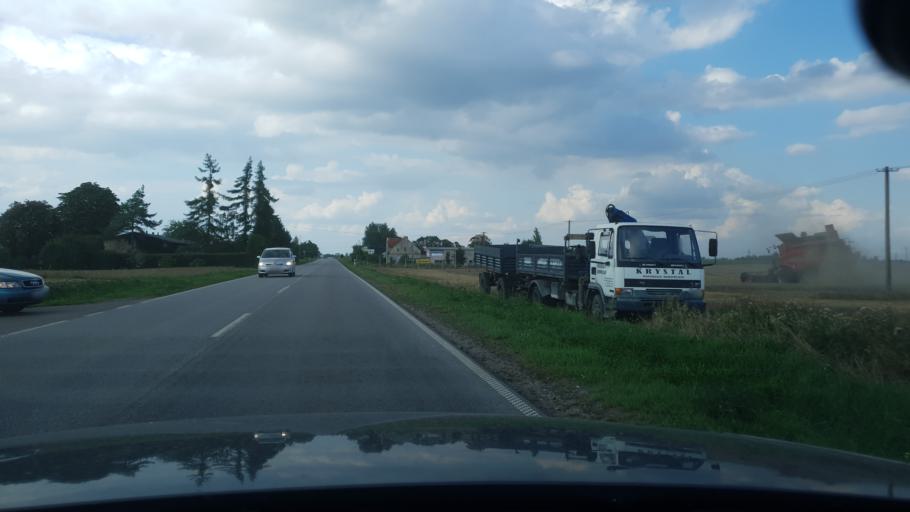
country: PL
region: Kujawsko-Pomorskie
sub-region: Powiat wabrzeski
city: Wabrzezno
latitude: 53.3112
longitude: 18.9350
